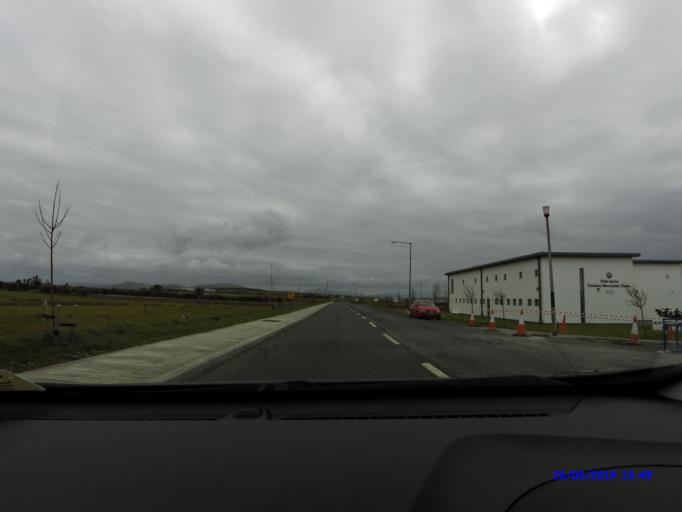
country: IE
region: Connaught
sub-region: Maigh Eo
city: Belmullet
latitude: 54.2153
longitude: -9.9780
